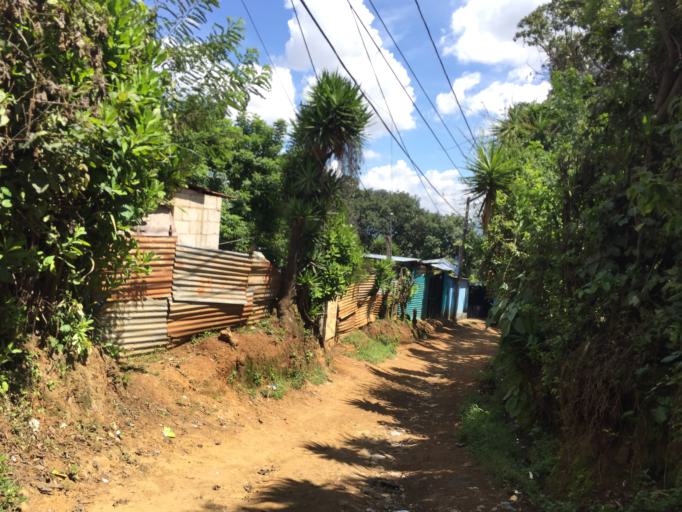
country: GT
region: Guatemala
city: Amatitlan
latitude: 14.5093
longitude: -90.6486
